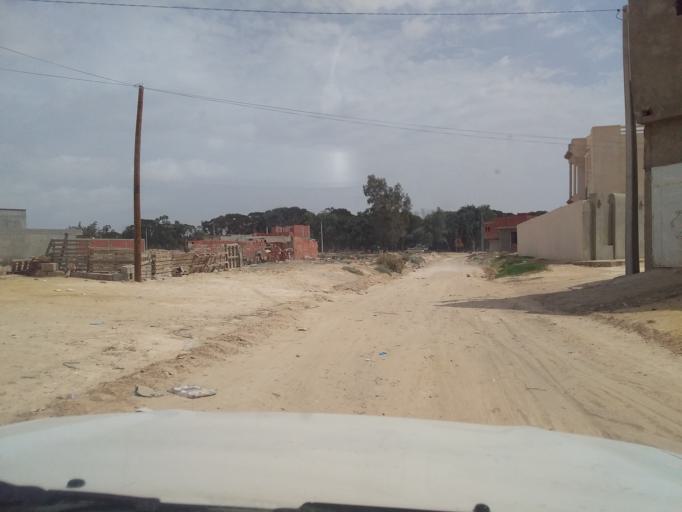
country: TN
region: Qabis
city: Matmata
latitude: 33.6216
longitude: 10.2732
